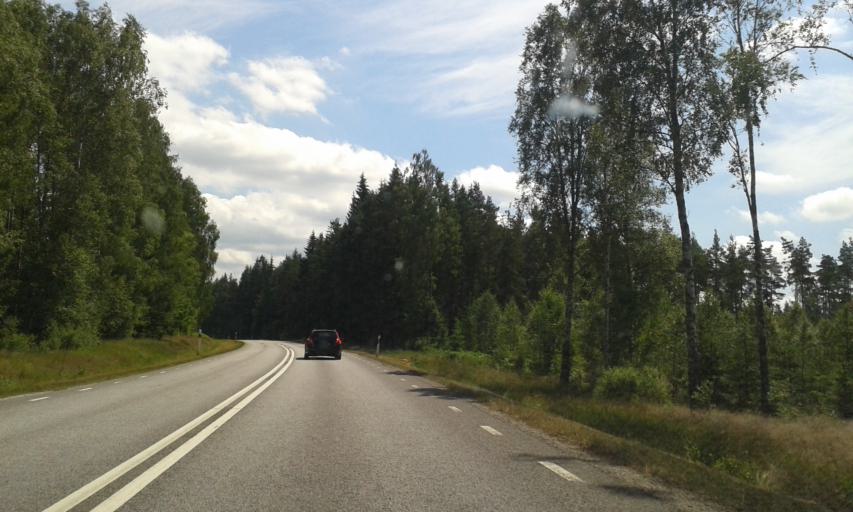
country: SE
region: Joenkoeping
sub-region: Varnamo Kommun
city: Rydaholm
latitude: 56.9765
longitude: 14.3103
